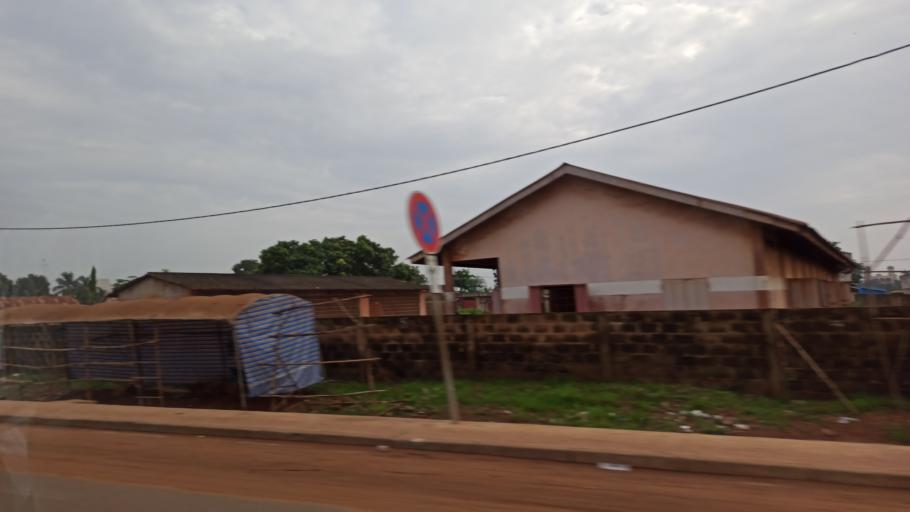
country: BJ
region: Queme
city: Porto-Novo
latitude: 6.5164
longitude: 2.6042
